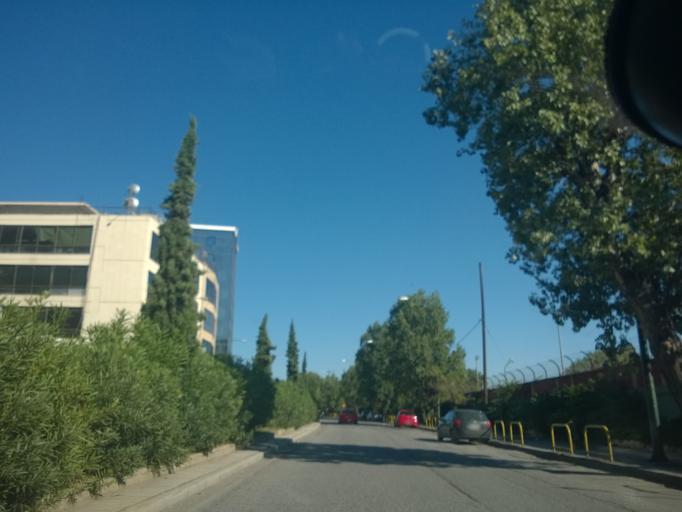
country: GR
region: Central Macedonia
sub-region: Nomos Thessalonikis
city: Thessaloniki
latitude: 40.6404
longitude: 22.9206
